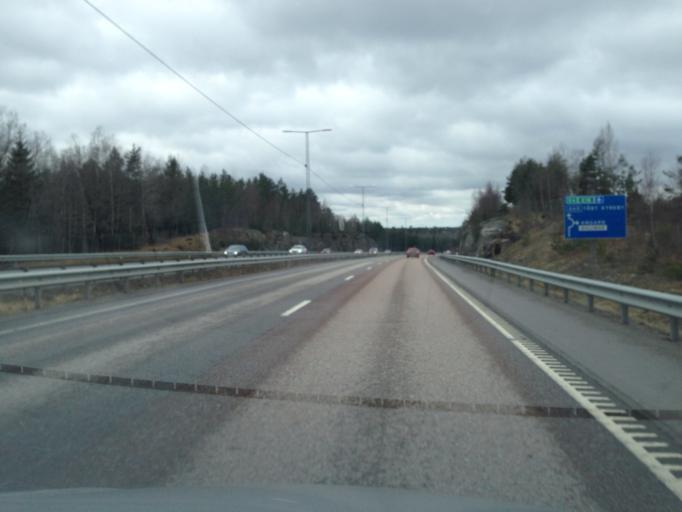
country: SE
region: Stockholm
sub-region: Vallentuna Kommun
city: Vallentuna
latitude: 59.4947
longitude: 18.1757
